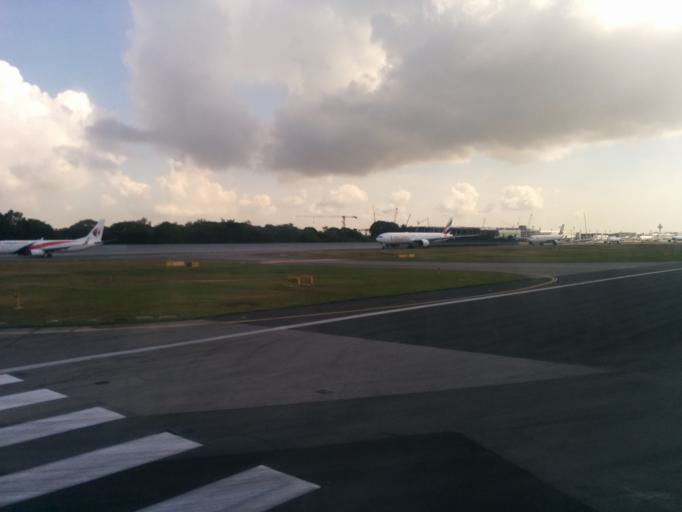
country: SG
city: Singapore
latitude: 1.3291
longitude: 103.9851
